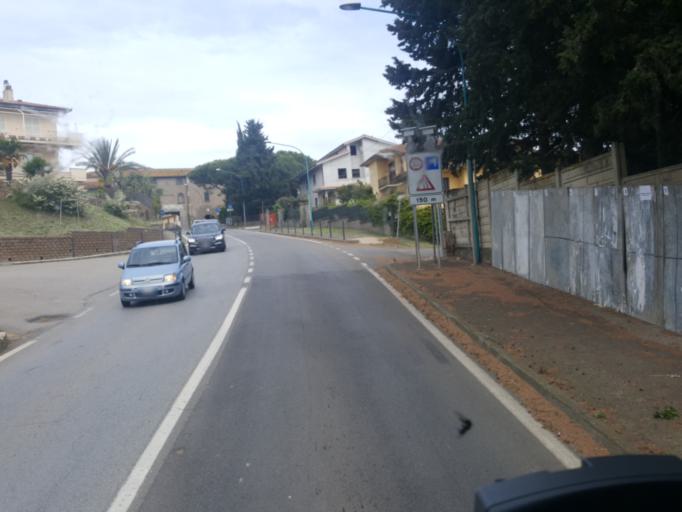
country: IT
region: Latium
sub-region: Provincia di Viterbo
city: Monte Romano
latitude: 42.2674
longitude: 11.8951
